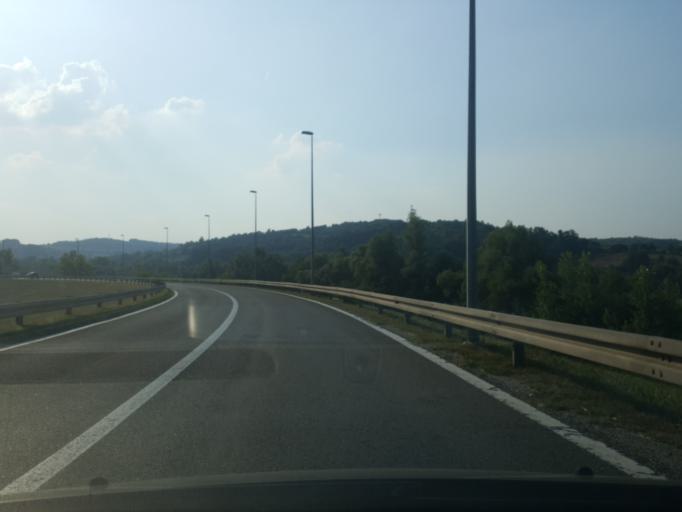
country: RS
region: Central Serbia
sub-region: Belgrade
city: Sopot
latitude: 44.5664
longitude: 20.6679
